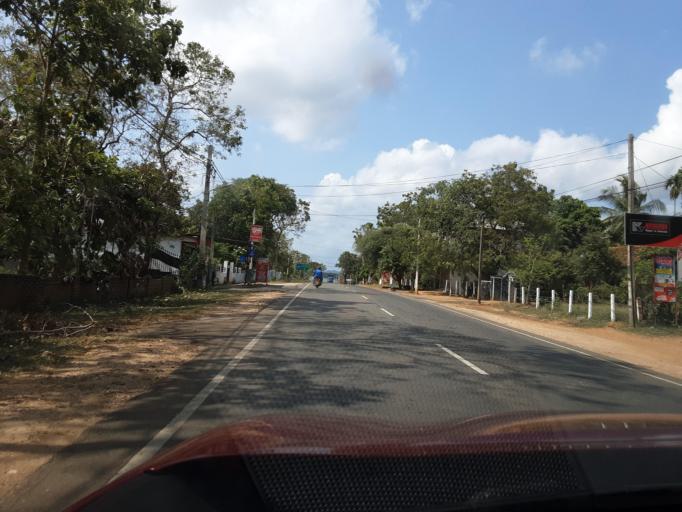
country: LK
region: Southern
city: Tangalla
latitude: 6.2798
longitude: 81.2300
